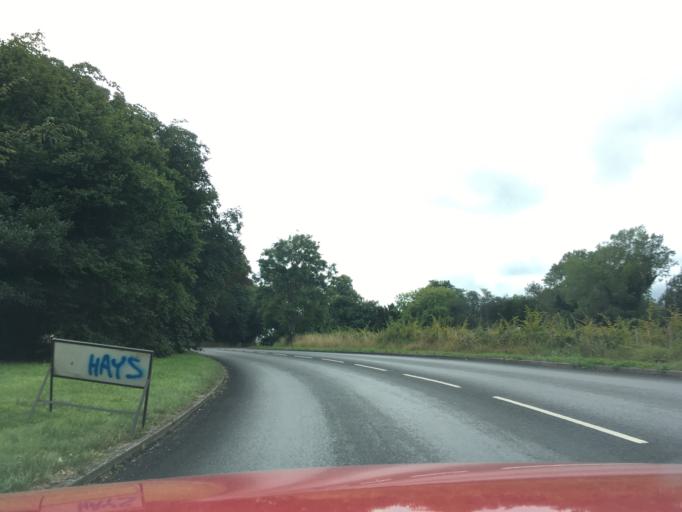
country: GB
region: England
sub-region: Kent
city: Marden
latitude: 51.1150
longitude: 0.4661
